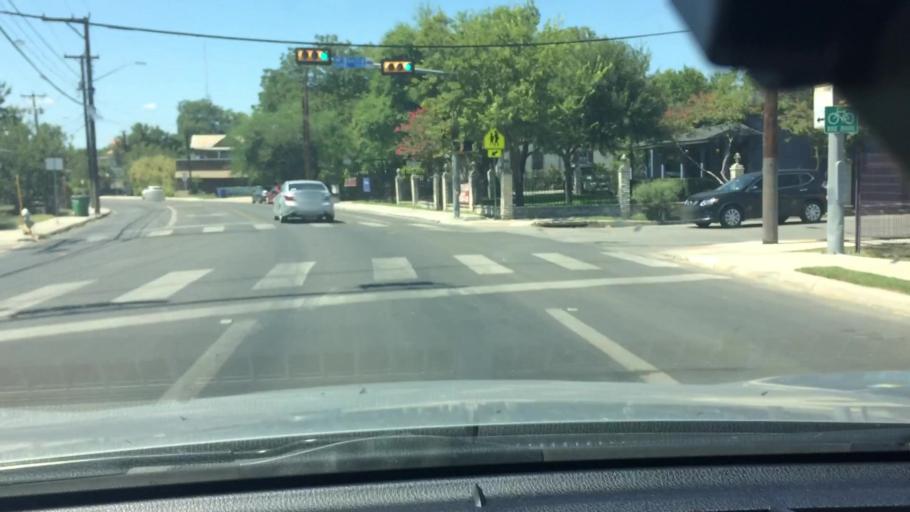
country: US
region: Texas
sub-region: Bexar County
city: San Antonio
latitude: 29.4348
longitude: -98.4996
